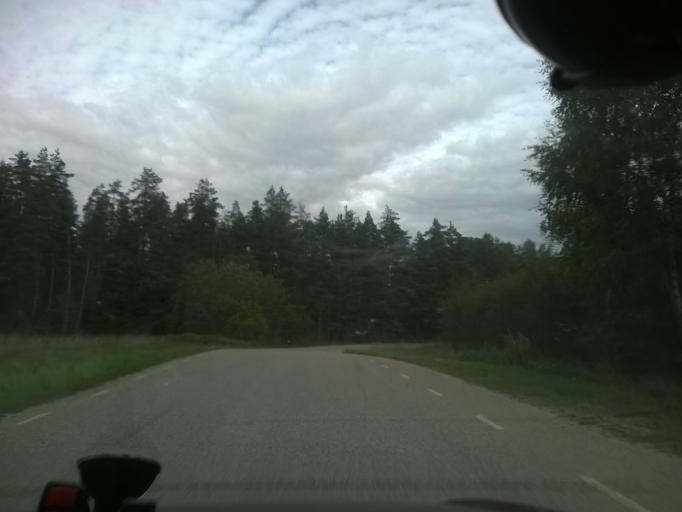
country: EE
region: Vorumaa
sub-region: Voru linn
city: Voru
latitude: 57.7546
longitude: 26.9823
